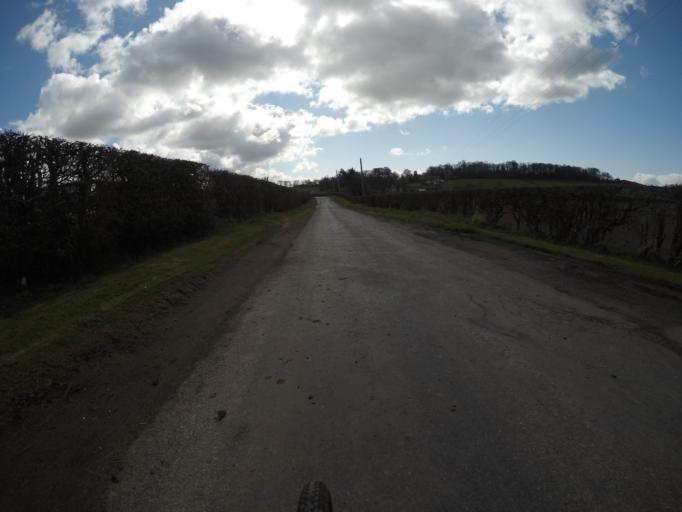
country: GB
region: Scotland
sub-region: South Ayrshire
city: Dundonald
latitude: 55.5874
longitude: -4.5765
